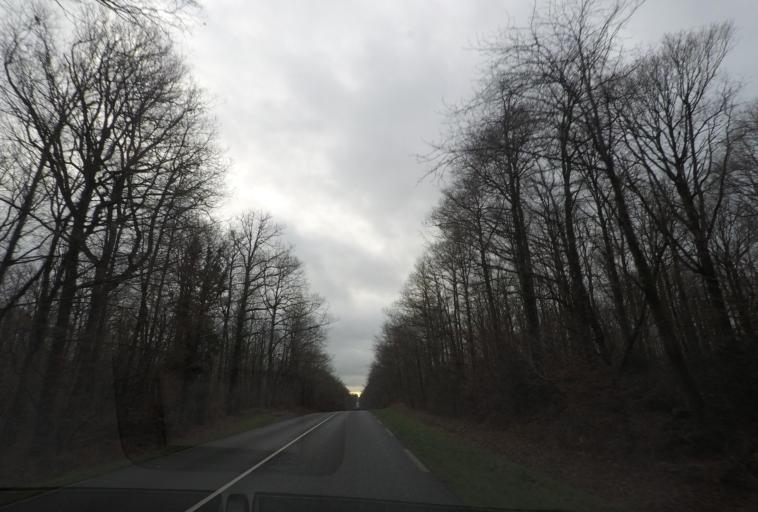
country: FR
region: Pays de la Loire
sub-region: Departement de la Sarthe
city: Vibraye
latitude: 48.0269
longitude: 0.7495
